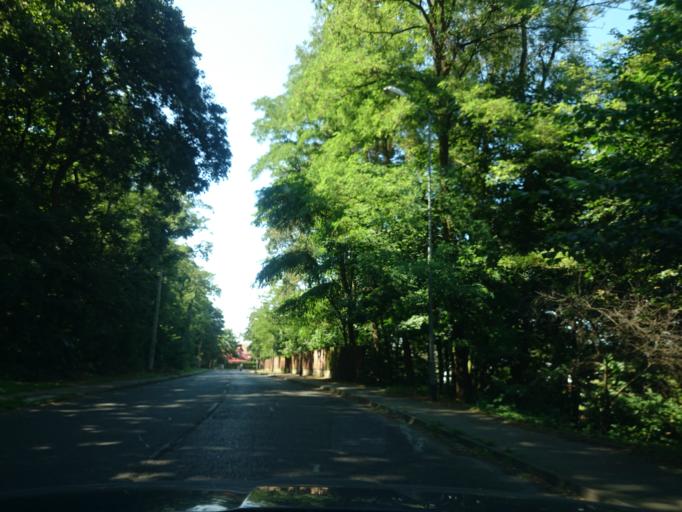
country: PL
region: West Pomeranian Voivodeship
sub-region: Powiat policki
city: Police
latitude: 53.5376
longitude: 14.5842
